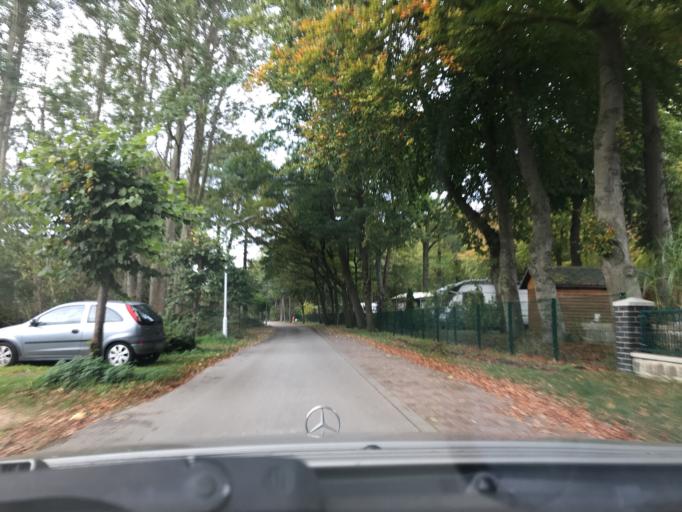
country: DE
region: Mecklenburg-Vorpommern
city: Loddin
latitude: 54.0316
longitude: 14.0379
